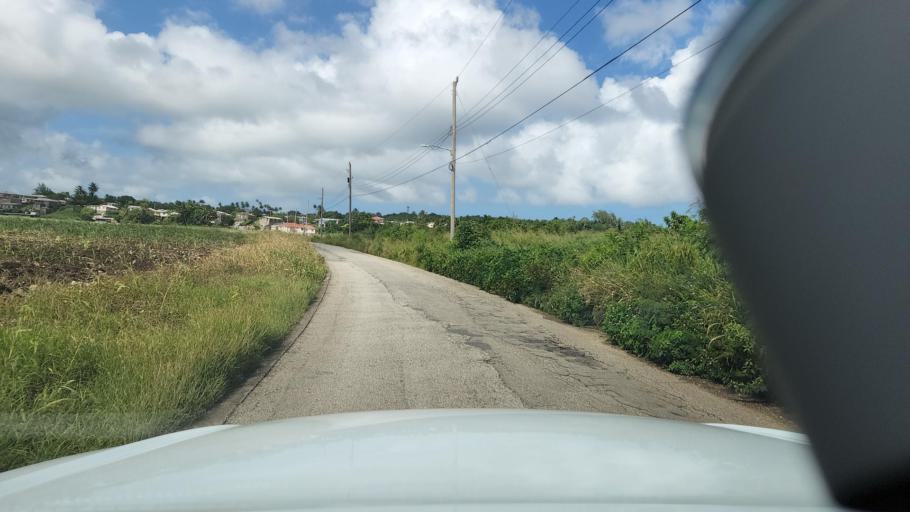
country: BB
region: Saint John
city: Four Cross Roads
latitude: 13.1911
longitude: -59.5072
